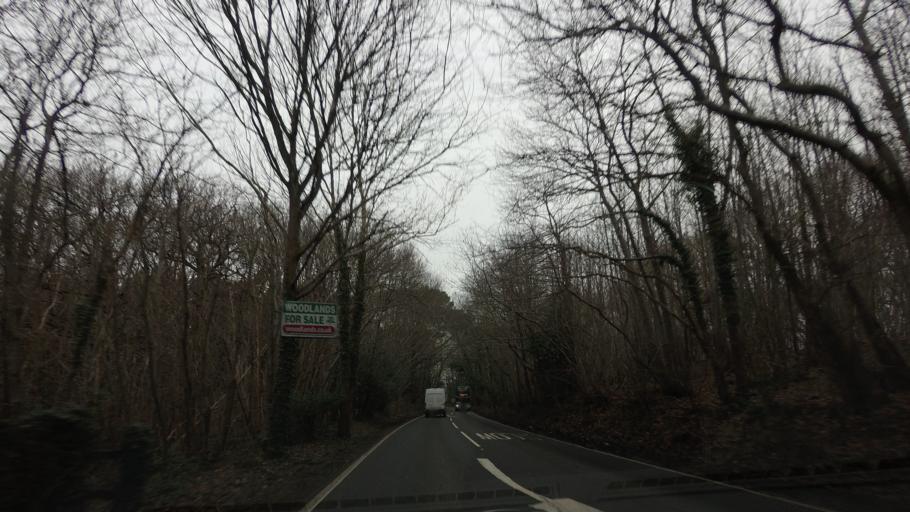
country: GB
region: England
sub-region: Kent
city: Staplehurst
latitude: 51.1282
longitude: 0.5609
